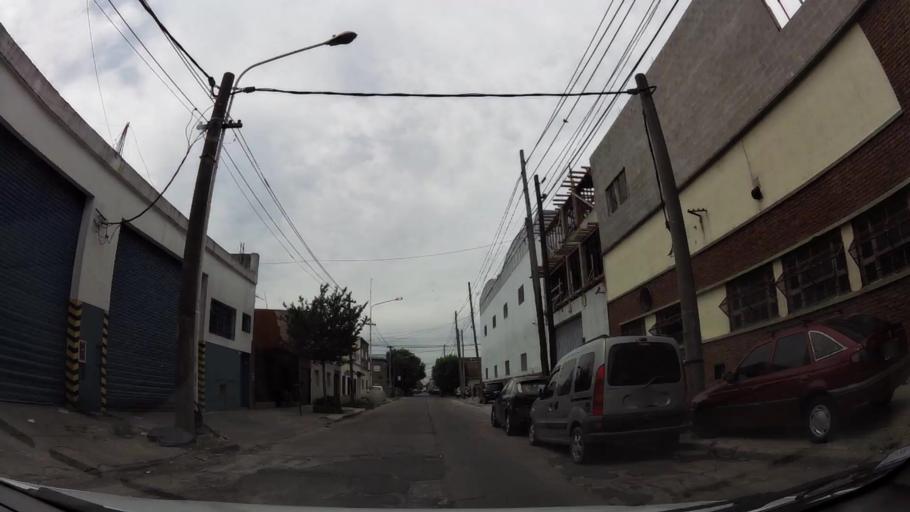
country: AR
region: Buenos Aires
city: San Justo
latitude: -34.6736
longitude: -58.5388
